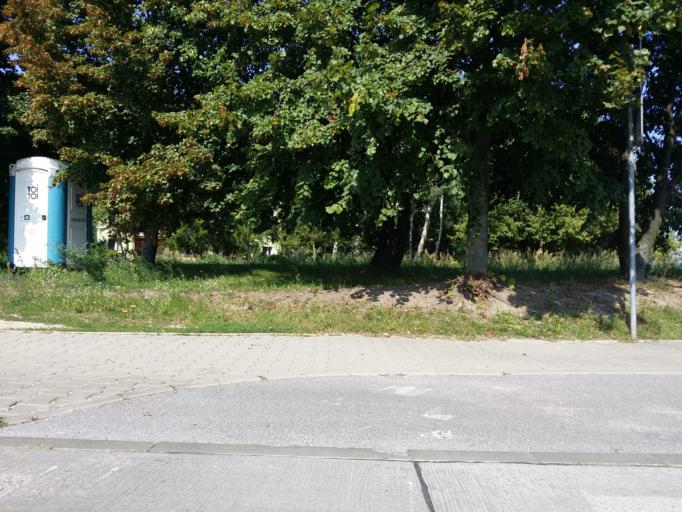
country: PL
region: Masovian Voivodeship
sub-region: Radom
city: Radom
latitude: 51.3730
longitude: 21.1638
